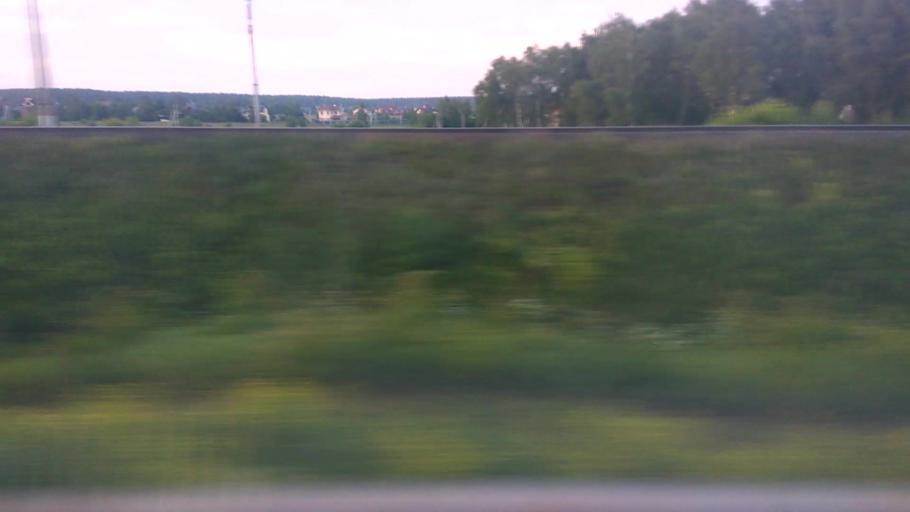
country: RU
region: Moskovskaya
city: Vostryakovo
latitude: 55.3721
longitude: 37.8224
